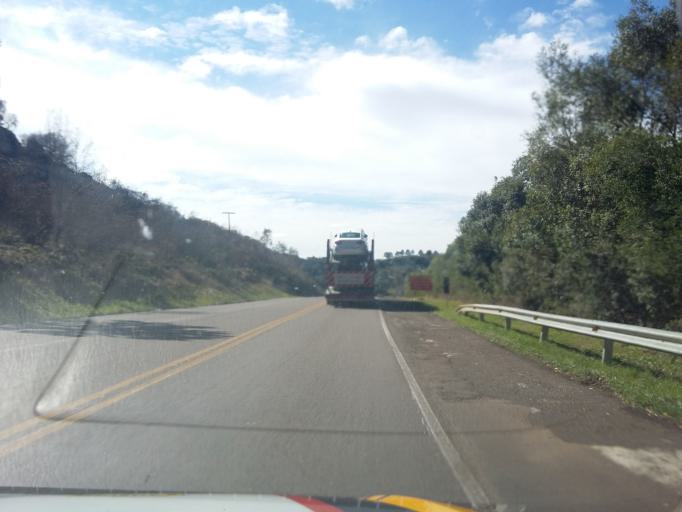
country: BR
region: Rio Grande do Sul
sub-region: Vacaria
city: Vacaria
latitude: -28.5904
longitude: -51.0298
